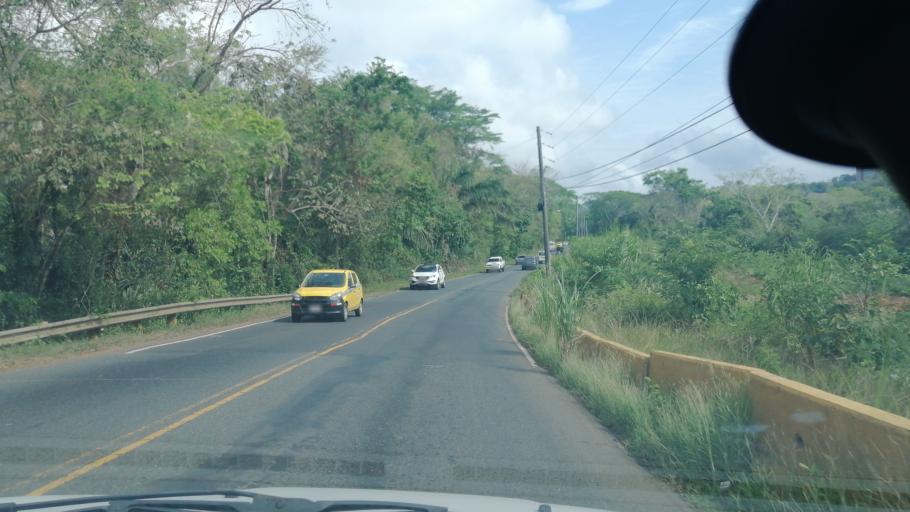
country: PA
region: Panama
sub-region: Distrito de Panama
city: Paraiso
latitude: 9.0413
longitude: -79.6344
